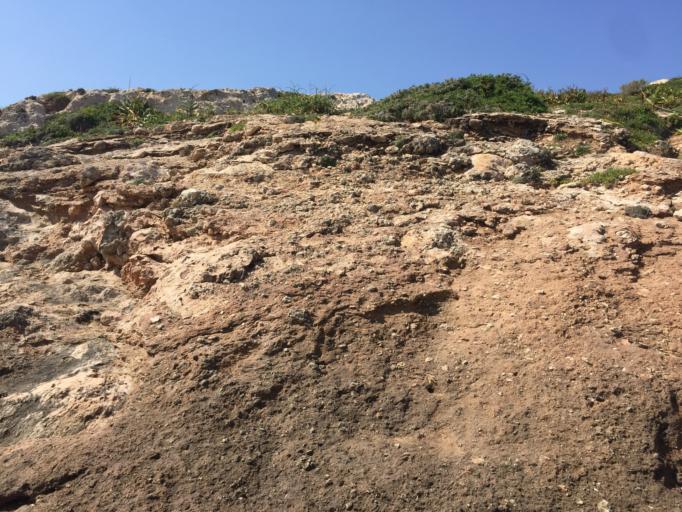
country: IT
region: Sicily
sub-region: Agrigento
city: Lampedusa
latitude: 35.4951
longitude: 12.6079
